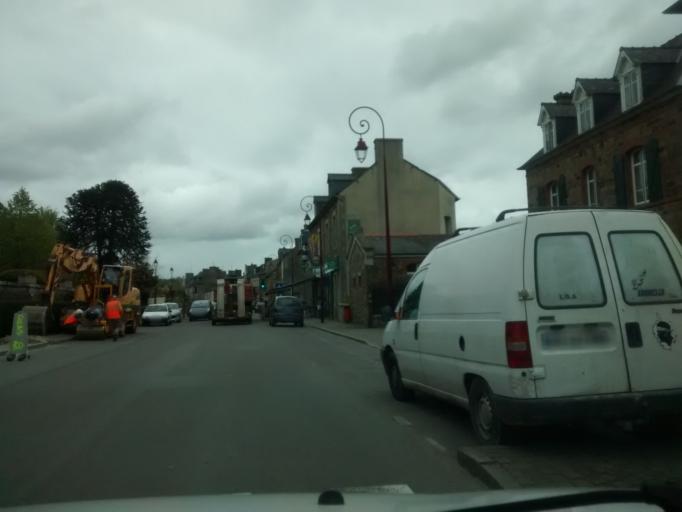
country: FR
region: Brittany
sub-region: Departement d'Ille-et-Vilaine
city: Saint-Pere
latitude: 48.5611
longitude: -1.9293
